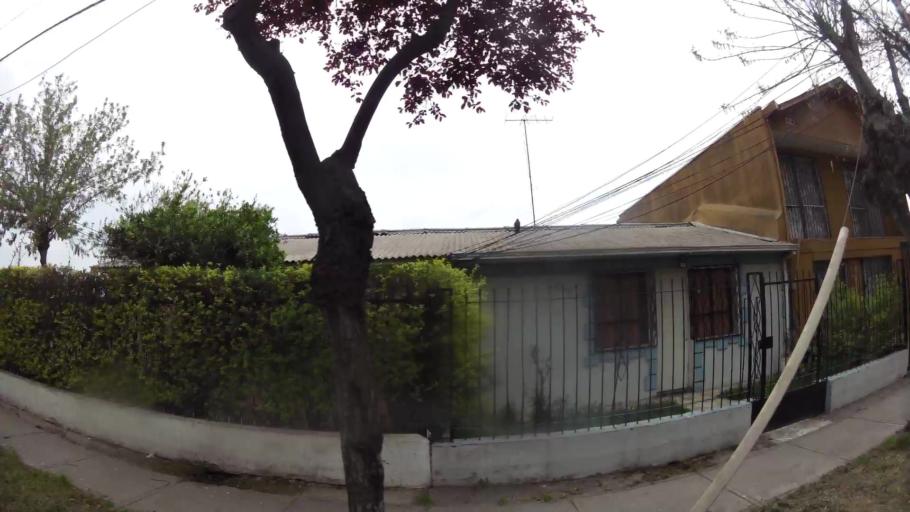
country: CL
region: Santiago Metropolitan
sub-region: Provincia de Santiago
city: Villa Presidente Frei, Nunoa, Santiago, Chile
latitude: -33.4702
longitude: -70.5927
